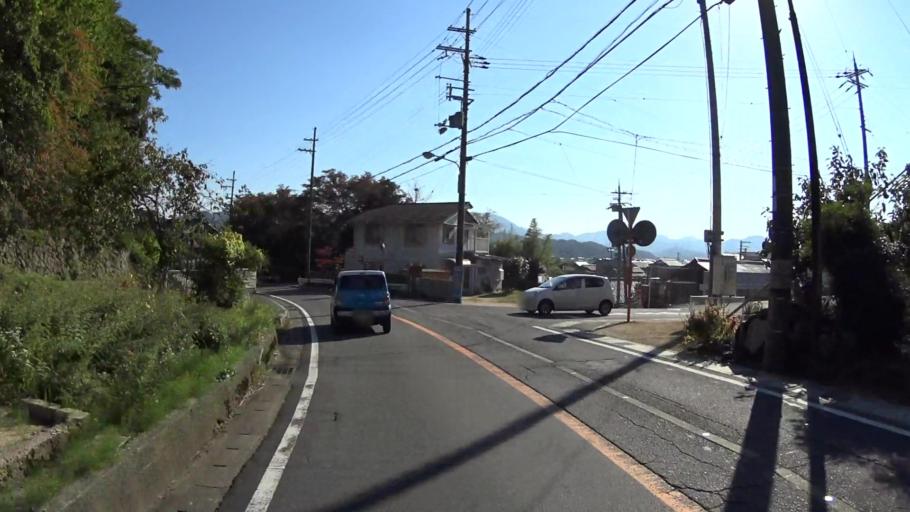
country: JP
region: Kyoto
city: Miyazu
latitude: 35.6156
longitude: 135.0605
